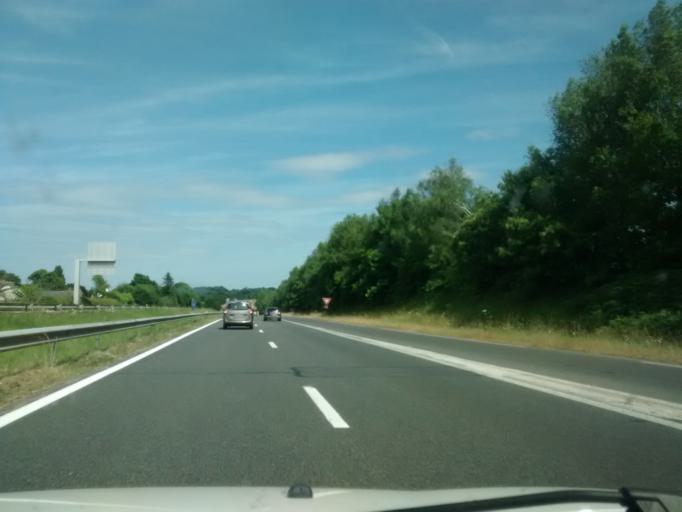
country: FR
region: Brittany
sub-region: Departement des Cotes-d'Armor
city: Plelo
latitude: 48.5314
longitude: -2.9334
